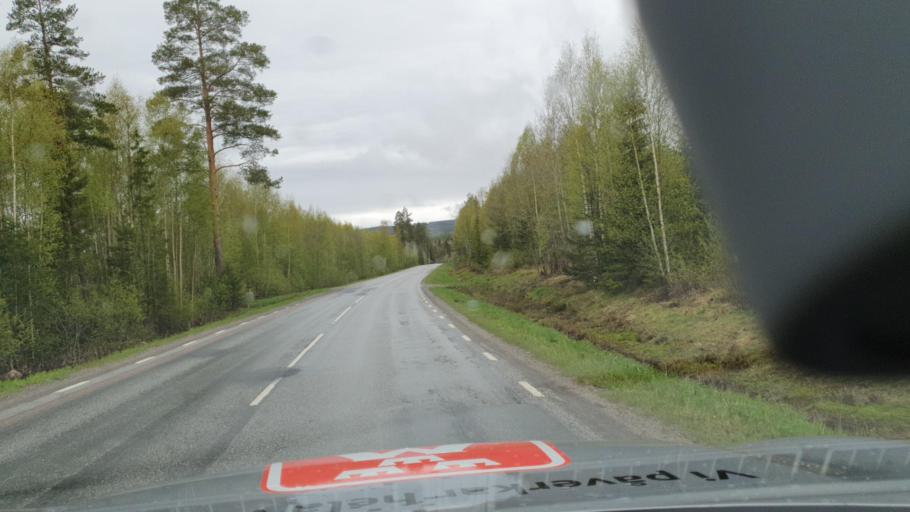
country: SE
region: Vaesternorrland
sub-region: OErnskoeldsviks Kommun
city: Bjasta
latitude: 63.3390
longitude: 18.5376
